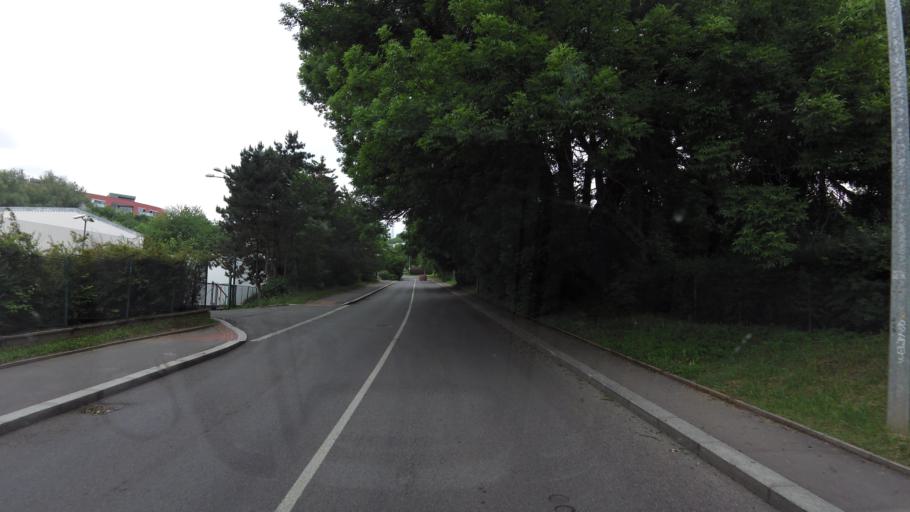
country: CZ
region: Praha
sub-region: Praha 1
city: Mala Strana
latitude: 50.0722
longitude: 14.3602
